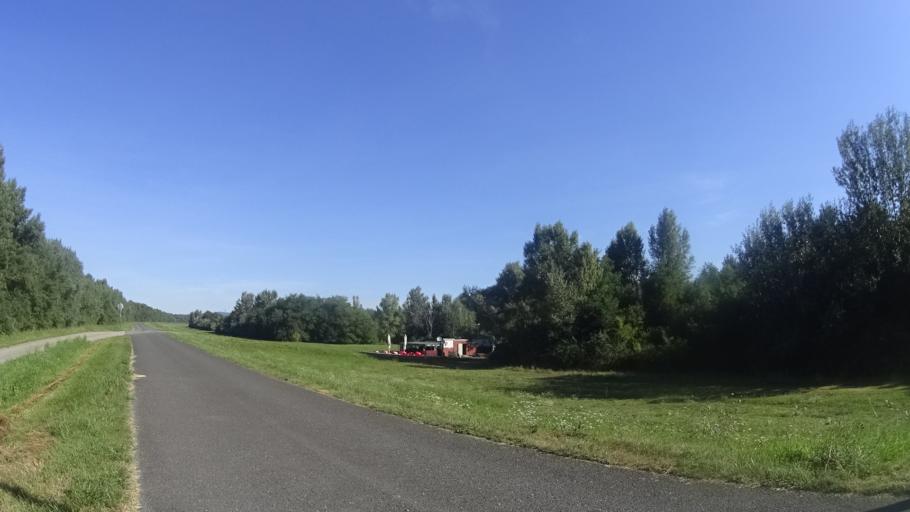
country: HU
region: Gyor-Moson-Sopron
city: Rajka
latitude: 48.0732
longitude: 17.1657
